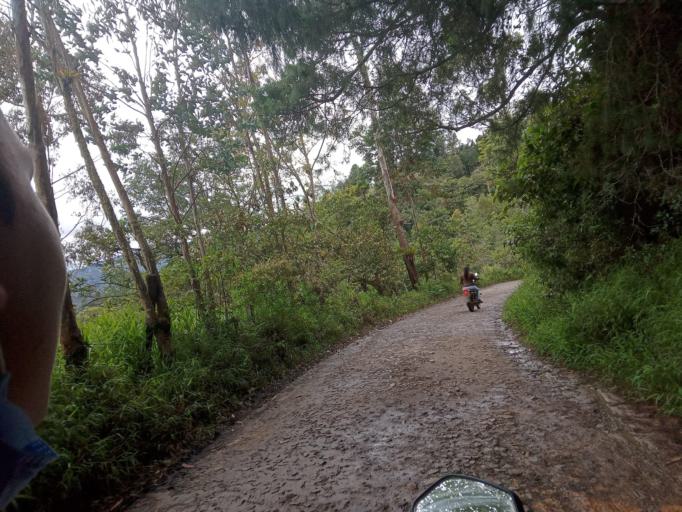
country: CO
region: Cundinamarca
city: Tenza
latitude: 5.1033
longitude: -73.4234
